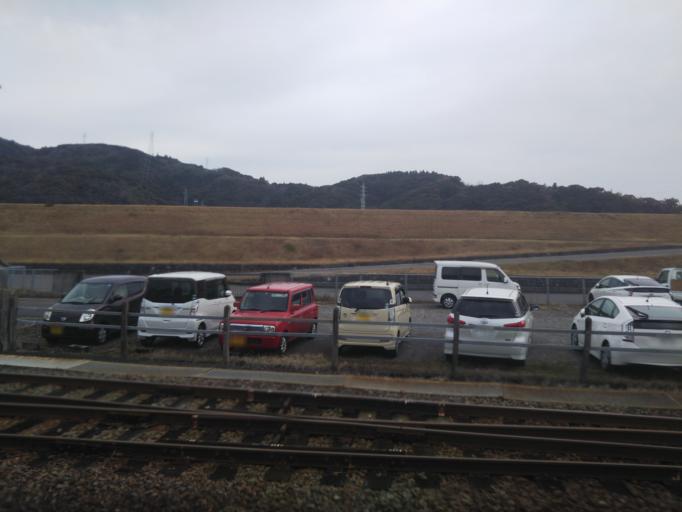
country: JP
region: Kochi
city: Nakamura
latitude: 32.9837
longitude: 132.9448
